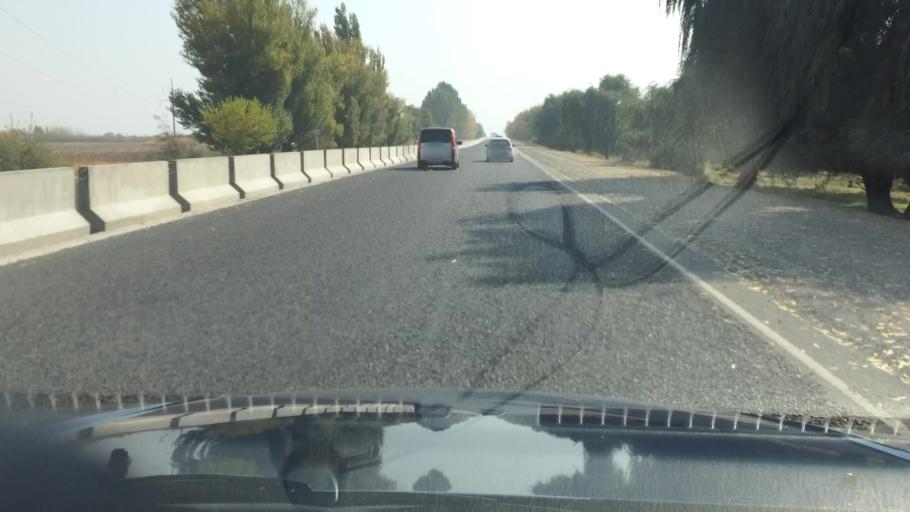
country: KG
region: Chuy
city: Kant
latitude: 42.9662
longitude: 74.9107
